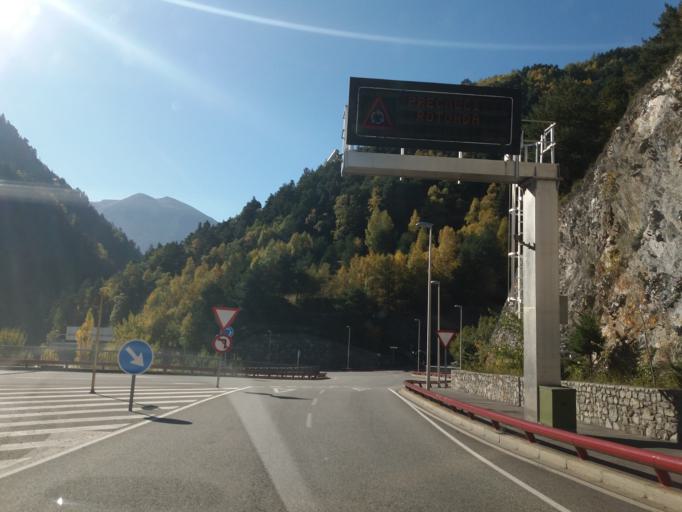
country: AD
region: La Massana
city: la Massana
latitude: 42.5309
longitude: 1.5199
